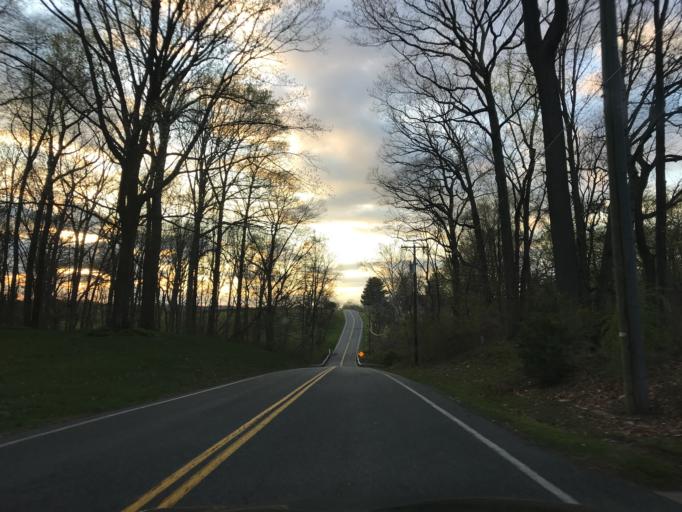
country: US
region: Maryland
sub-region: Harford County
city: Bel Air South
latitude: 39.5210
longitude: -76.3041
